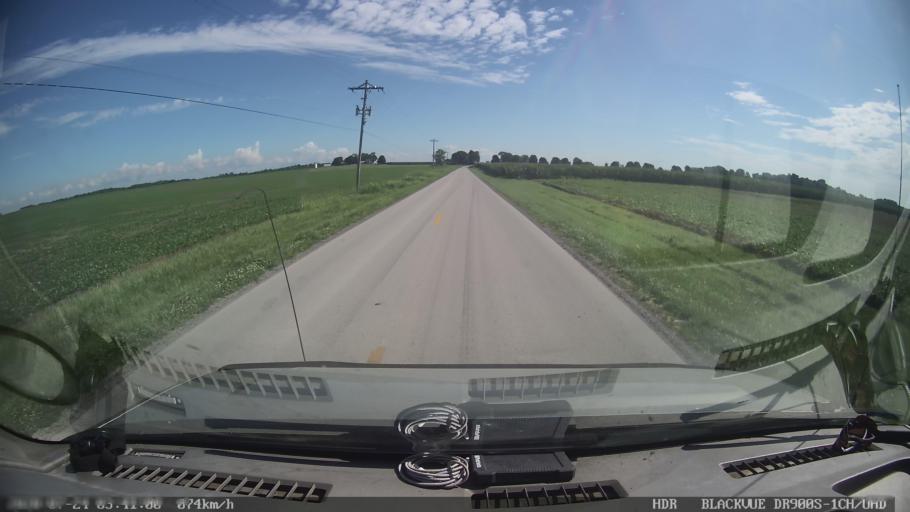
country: US
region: Kentucky
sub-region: Todd County
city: Guthrie
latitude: 36.7254
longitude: -87.2619
